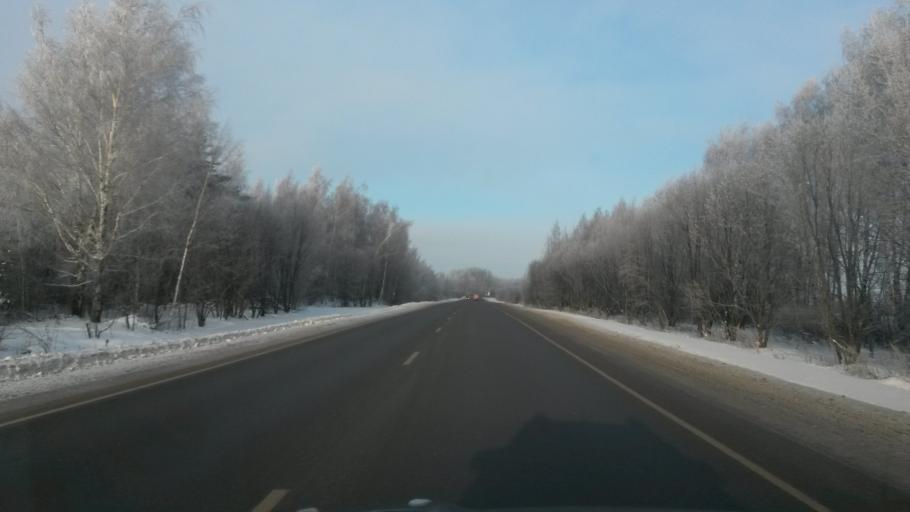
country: RU
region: Vladimir
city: Bogolyubovo
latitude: 56.2071
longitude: 40.4428
